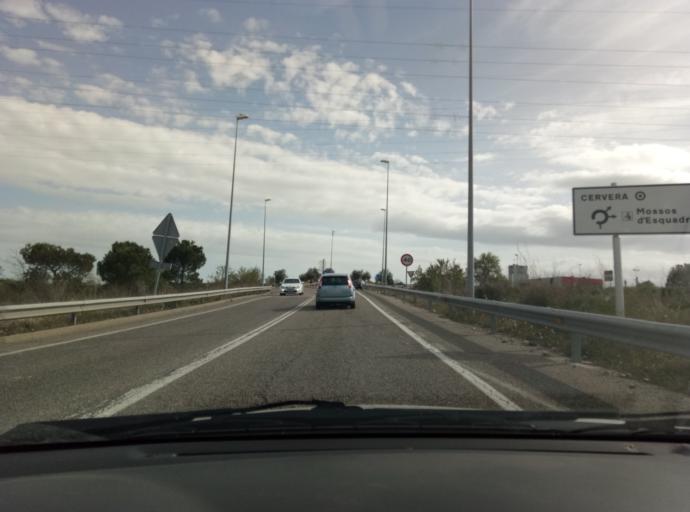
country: ES
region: Catalonia
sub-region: Provincia de Lleida
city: Cervera
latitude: 41.6793
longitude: 1.2846
